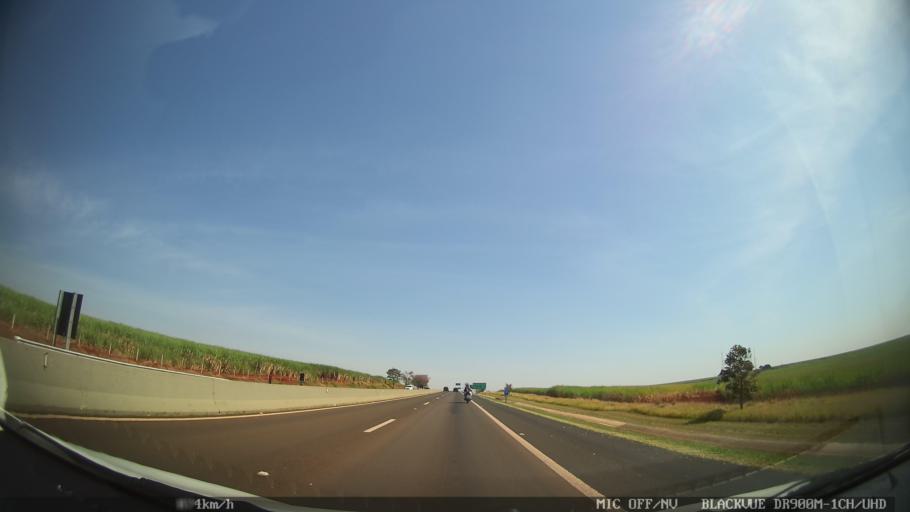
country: BR
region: Sao Paulo
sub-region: Ribeirao Preto
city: Ribeirao Preto
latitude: -21.1661
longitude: -47.8892
